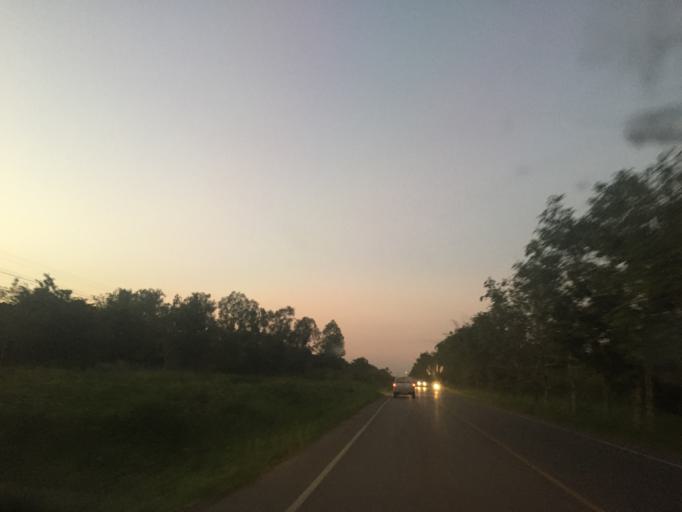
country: TH
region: Chiang Mai
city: Saraphi
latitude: 18.7227
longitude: 99.0365
